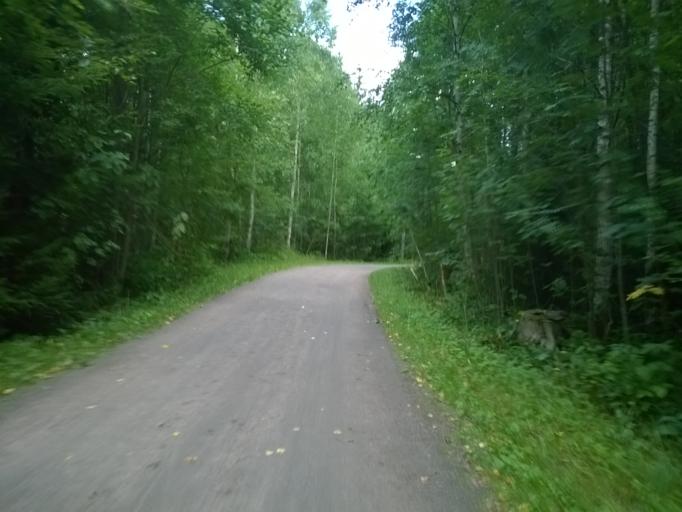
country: FI
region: Uusimaa
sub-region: Helsinki
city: Helsinki
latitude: 60.2565
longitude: 24.9090
